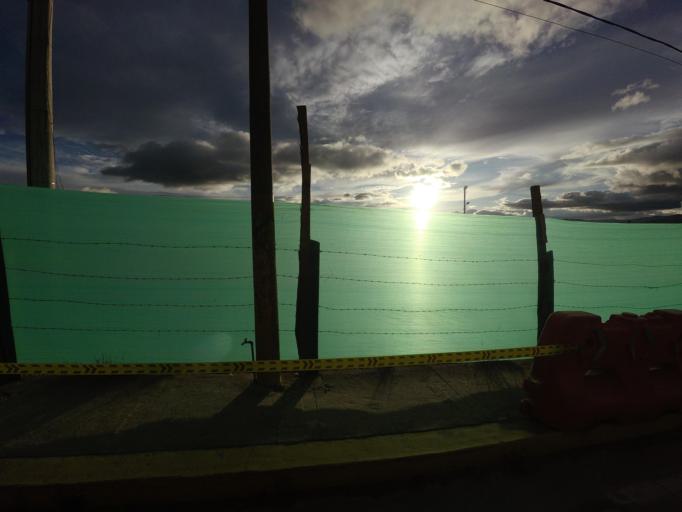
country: CO
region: Cundinamarca
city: Chia
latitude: 4.8355
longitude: -74.0289
